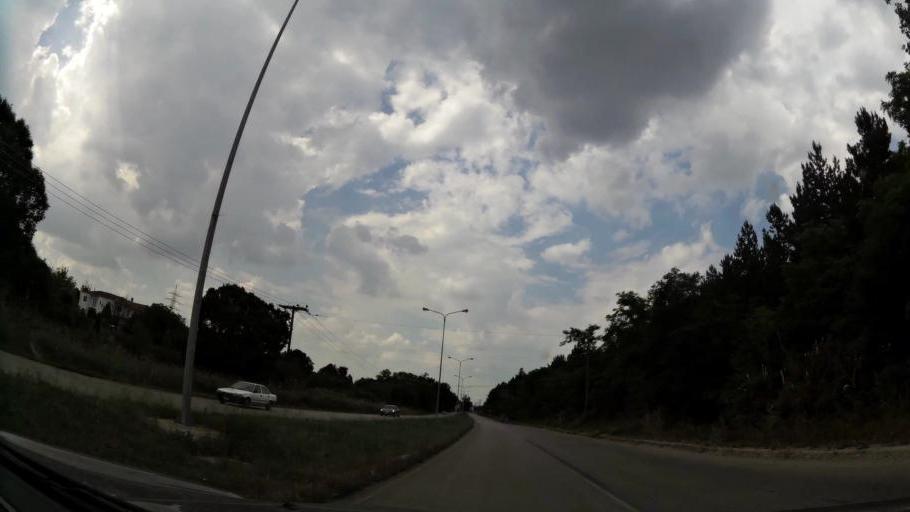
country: GR
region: West Macedonia
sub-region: Nomos Kozanis
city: Koila
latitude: 40.3304
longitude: 21.8273
